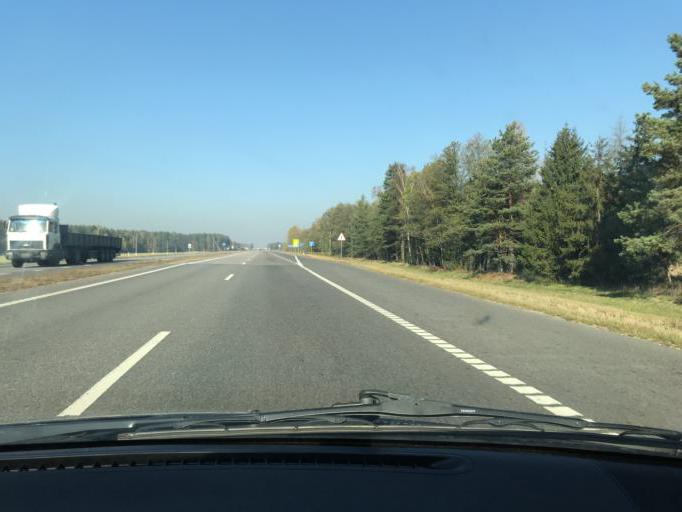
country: BY
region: Minsk
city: Slutsk
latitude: 53.3404
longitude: 27.5253
